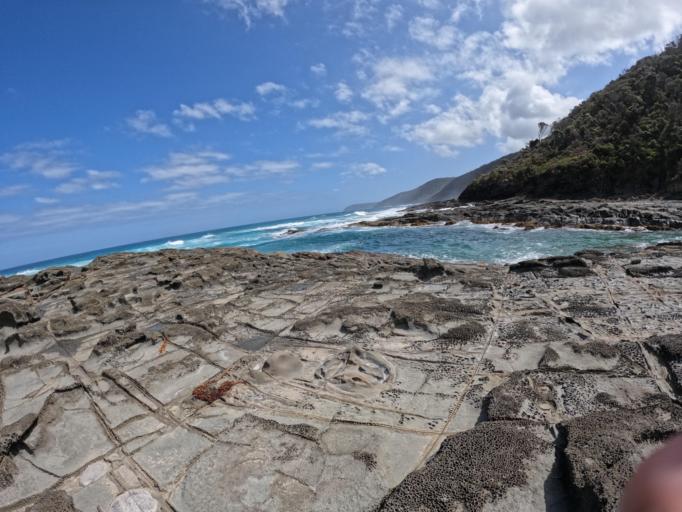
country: AU
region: Victoria
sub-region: Colac-Otway
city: Apollo Bay
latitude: -38.7928
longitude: 143.6230
